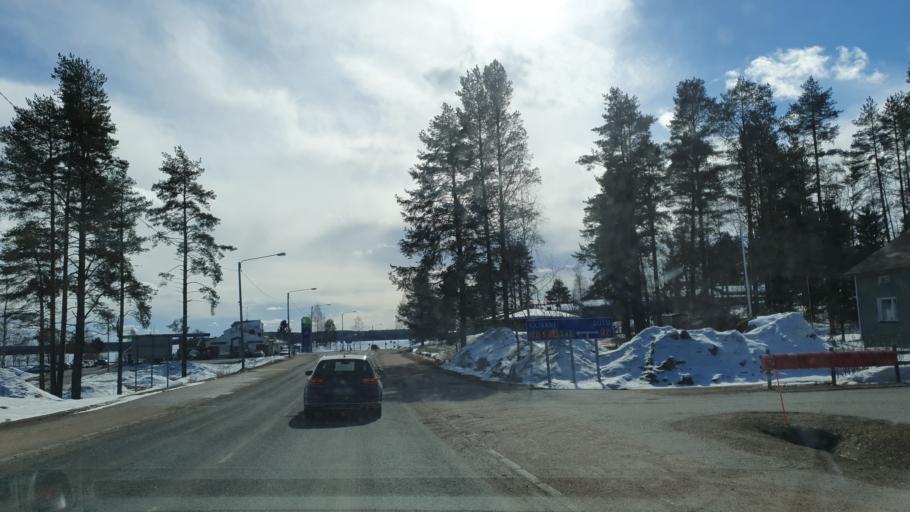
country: FI
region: Kainuu
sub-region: Kajaani
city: Paltamo
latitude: 64.4061
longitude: 27.8385
